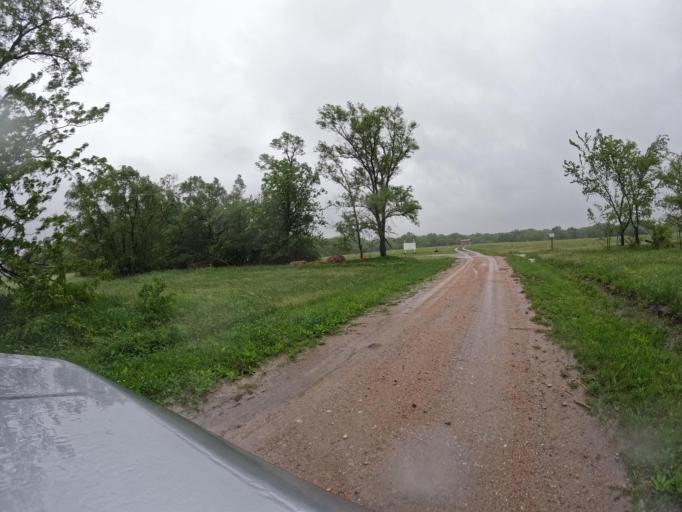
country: US
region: Nebraska
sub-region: Gage County
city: Wymore
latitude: 40.1427
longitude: -96.6682
